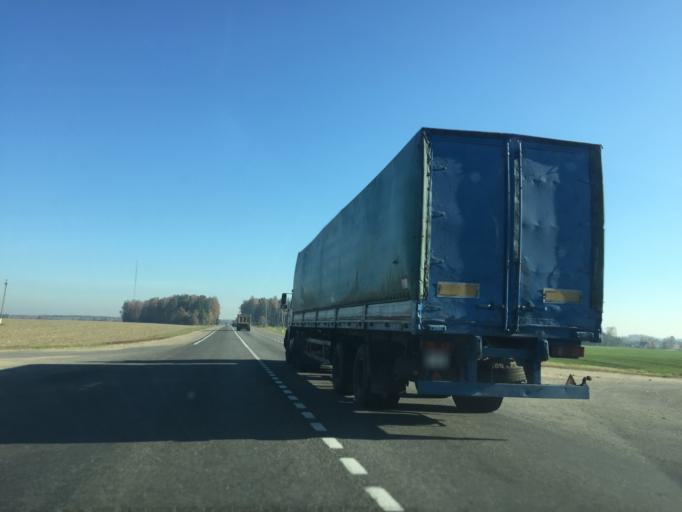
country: BY
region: Mogilev
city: Palykavichy Pyershyya
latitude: 53.9737
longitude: 30.2815
